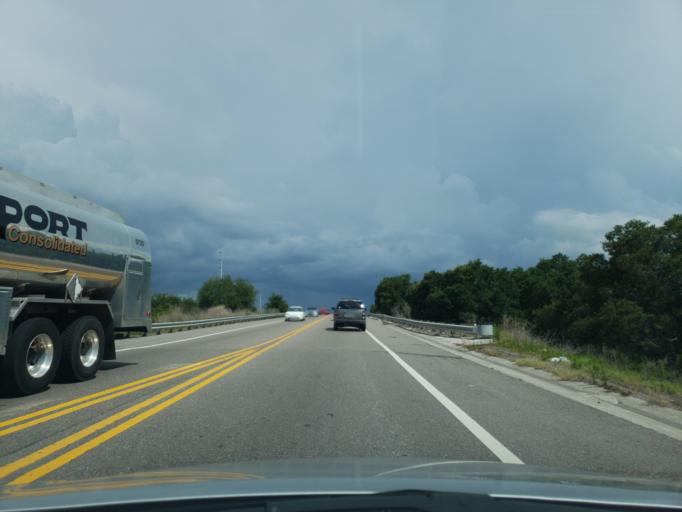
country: US
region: Florida
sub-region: Hillsborough County
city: Progress Village
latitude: 27.8964
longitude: -82.3498
